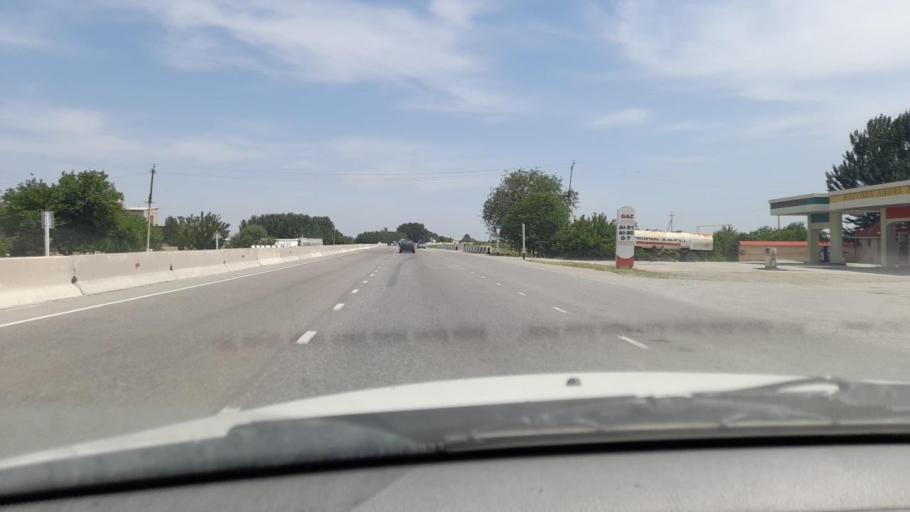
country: UZ
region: Navoiy
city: Karmana Shahri
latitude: 40.1274
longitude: 65.4547
